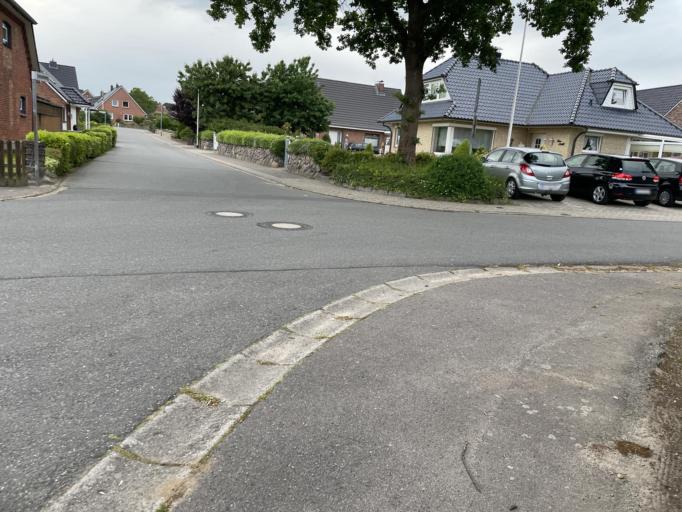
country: DE
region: Schleswig-Holstein
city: Mildstedt
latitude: 54.4620
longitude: 9.0933
